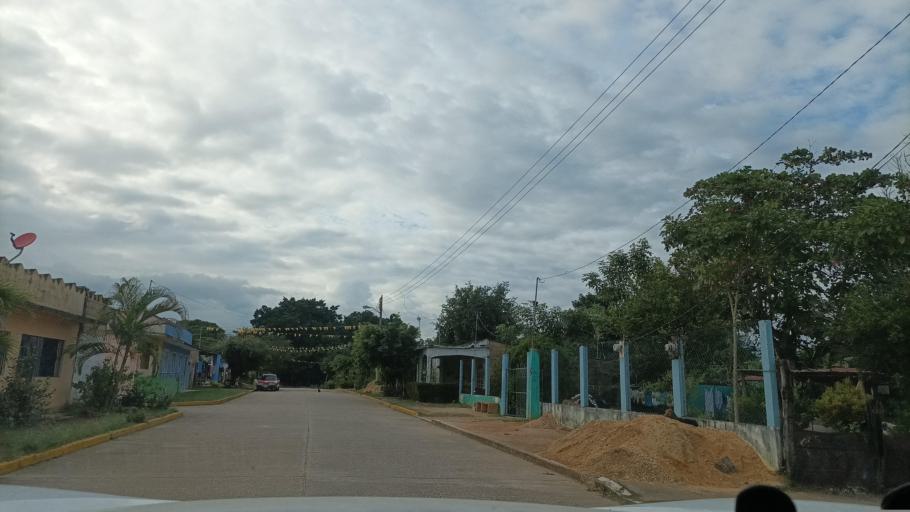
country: MX
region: Veracruz
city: Oluta
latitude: 17.8938
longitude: -94.8699
